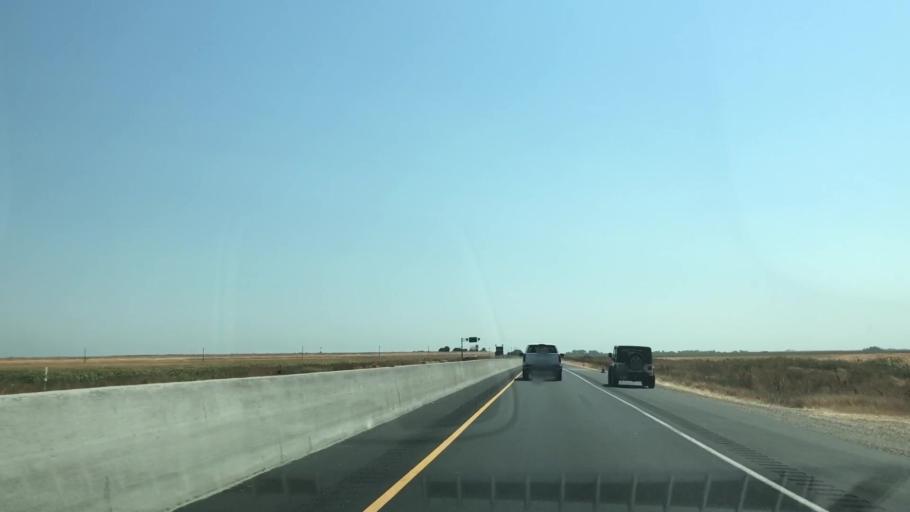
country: US
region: California
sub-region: Solano County
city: Rio Vista
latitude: 38.1212
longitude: -121.5697
